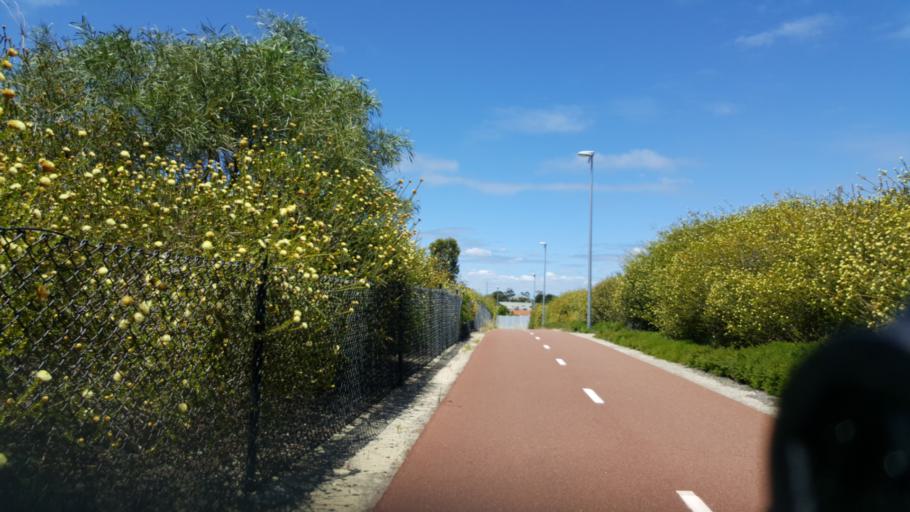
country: AU
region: Western Australia
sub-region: Bayswater
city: Bedford
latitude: -31.8688
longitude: 115.8829
